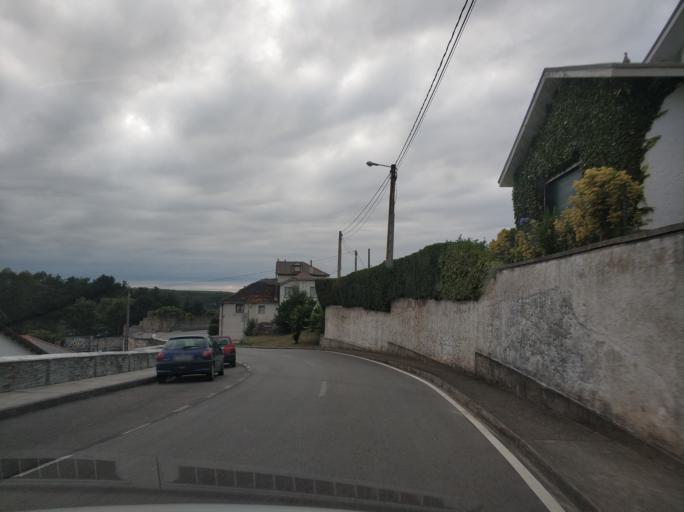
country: ES
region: Asturias
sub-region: Province of Asturias
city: Navia
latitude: 43.5473
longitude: -6.5310
